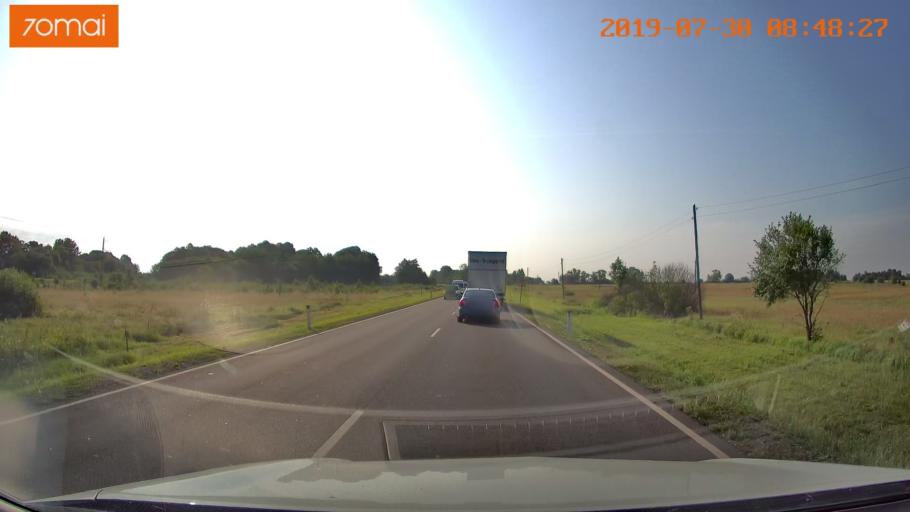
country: RU
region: Kaliningrad
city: Chernyakhovsk
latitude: 54.6176
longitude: 21.9059
